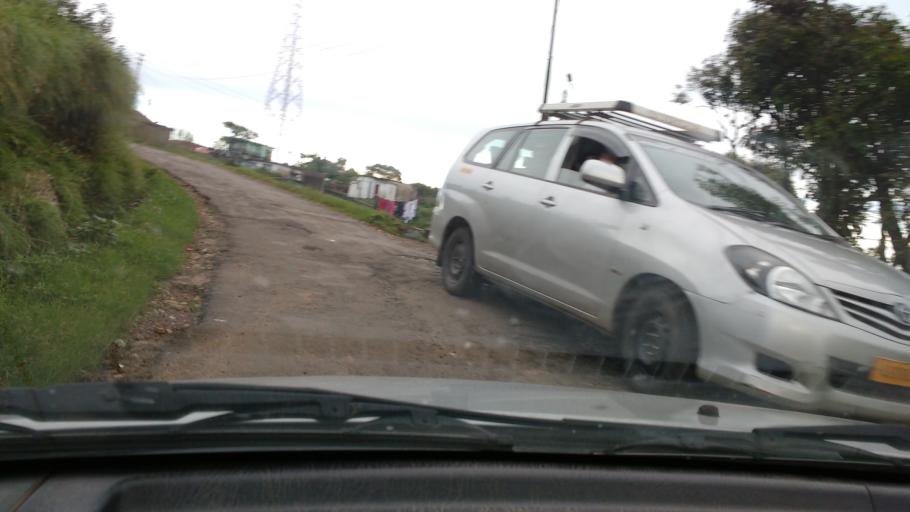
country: IN
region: Meghalaya
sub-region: East Khasi Hills
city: Cherrapunji
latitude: 25.2845
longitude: 91.7156
